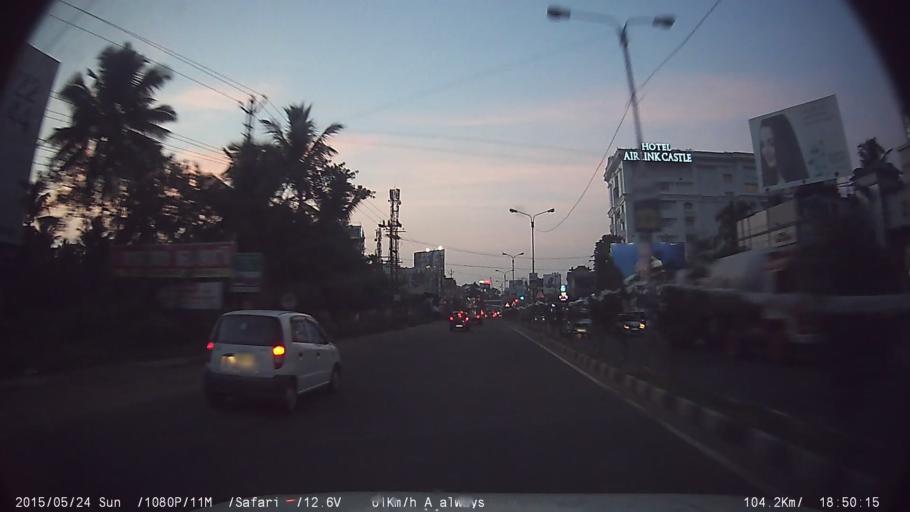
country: IN
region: Kerala
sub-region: Ernakulam
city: Aluva
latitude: 10.1539
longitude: 76.3546
